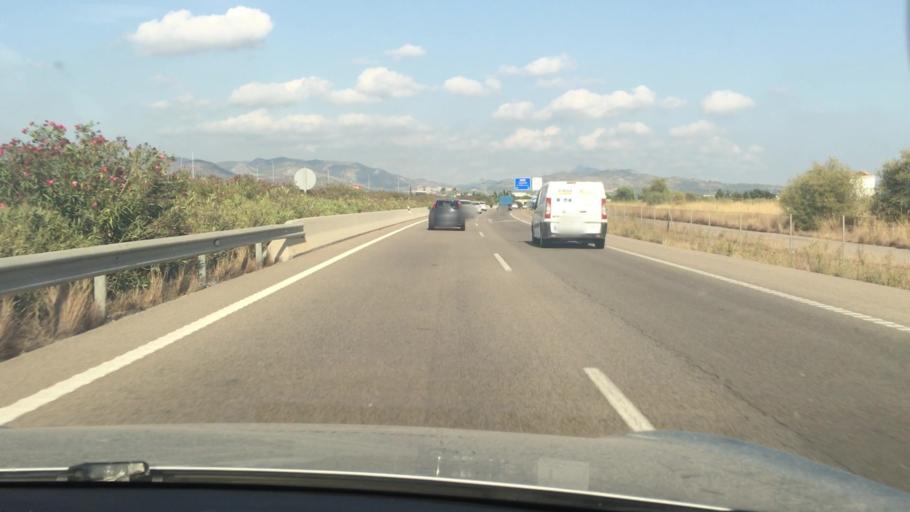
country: ES
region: Valencia
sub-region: Provincia de Castello
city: Vila-real
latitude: 39.9768
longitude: -0.1477
